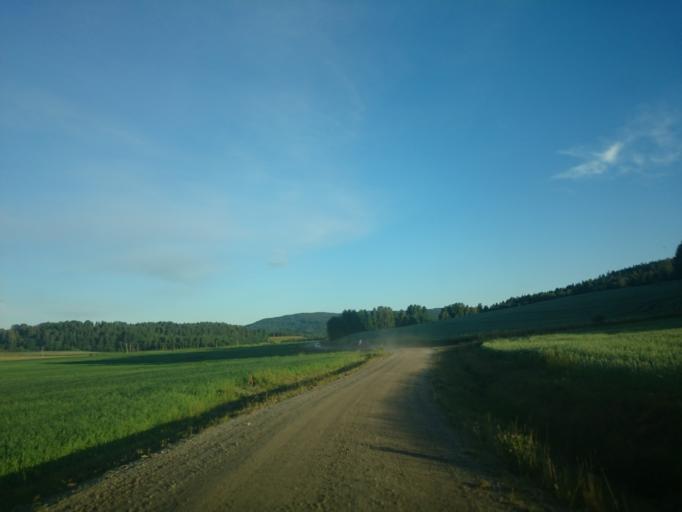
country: SE
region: Vaesternorrland
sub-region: Kramfors Kommun
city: Bollstabruk
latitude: 63.0703
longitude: 17.7341
